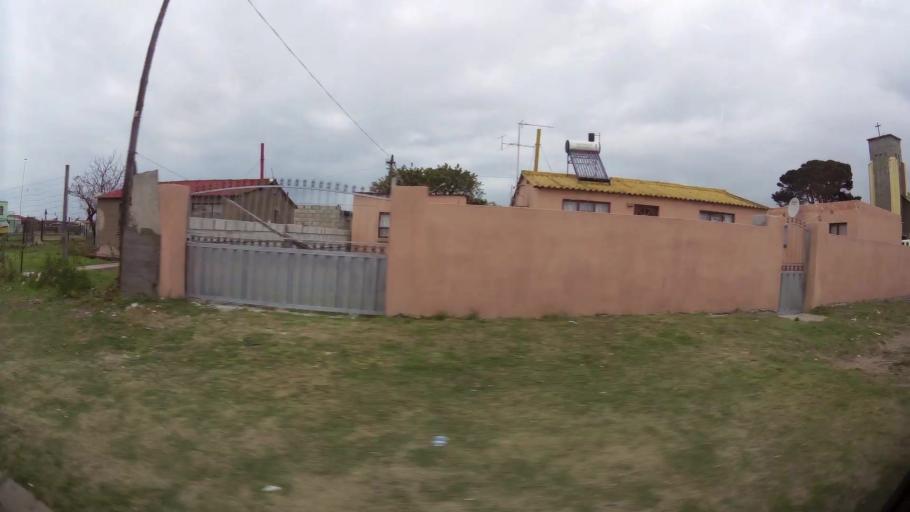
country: ZA
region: Eastern Cape
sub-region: Nelson Mandela Bay Metropolitan Municipality
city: Port Elizabeth
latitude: -33.8772
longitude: 25.5885
